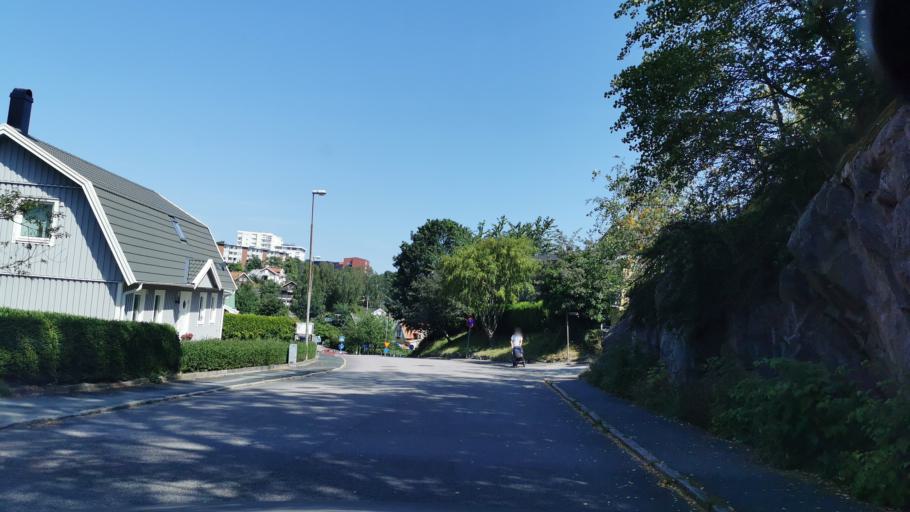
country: SE
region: Vaestra Goetaland
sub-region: Goteborg
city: Goeteborg
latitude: 57.6767
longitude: 11.9852
